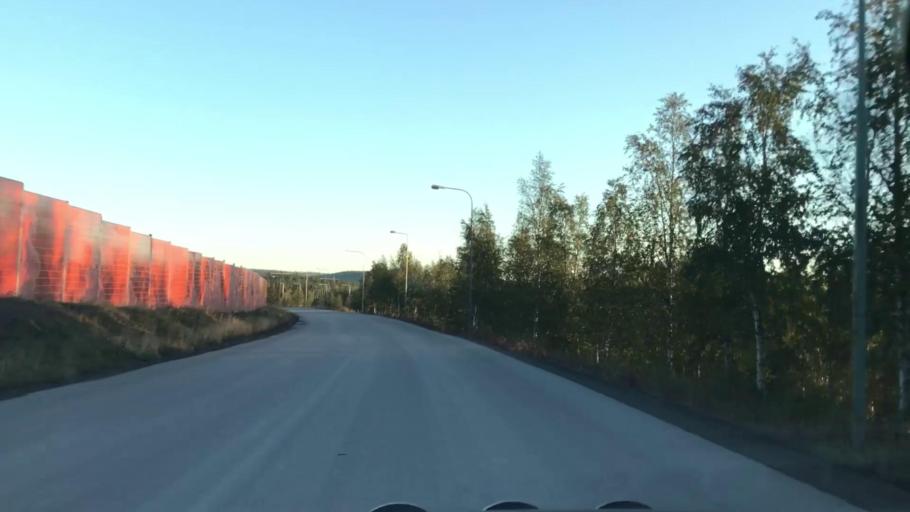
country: SE
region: Norrbotten
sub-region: Gallivare Kommun
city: Malmberget
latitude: 67.6493
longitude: 21.0189
